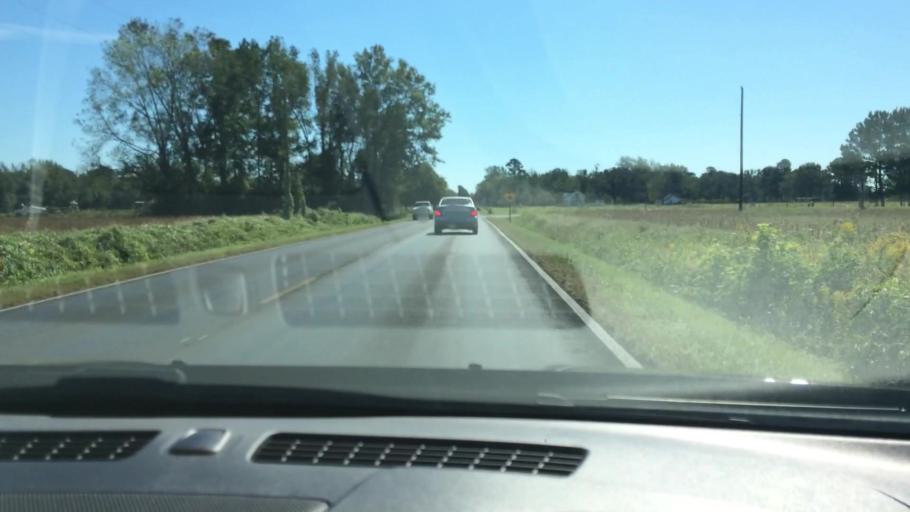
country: US
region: North Carolina
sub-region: Pitt County
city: Grifton
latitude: 35.3629
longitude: -77.3474
